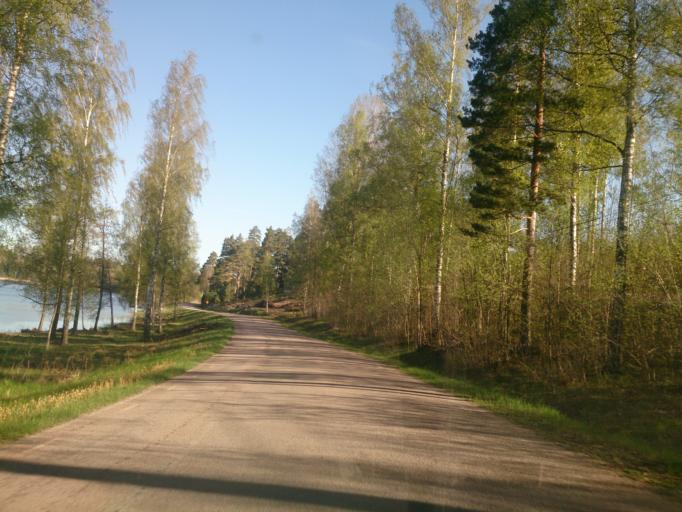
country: SE
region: OEstergoetland
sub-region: Linkopings Kommun
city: Ljungsbro
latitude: 58.5692
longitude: 15.5145
